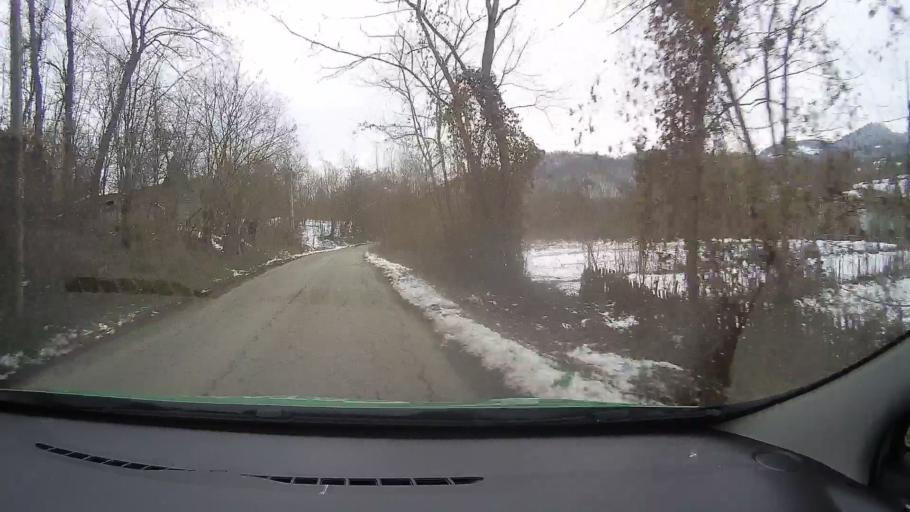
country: RO
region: Hunedoara
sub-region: Comuna Balsa
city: Balsa
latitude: 46.0386
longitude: 23.0753
